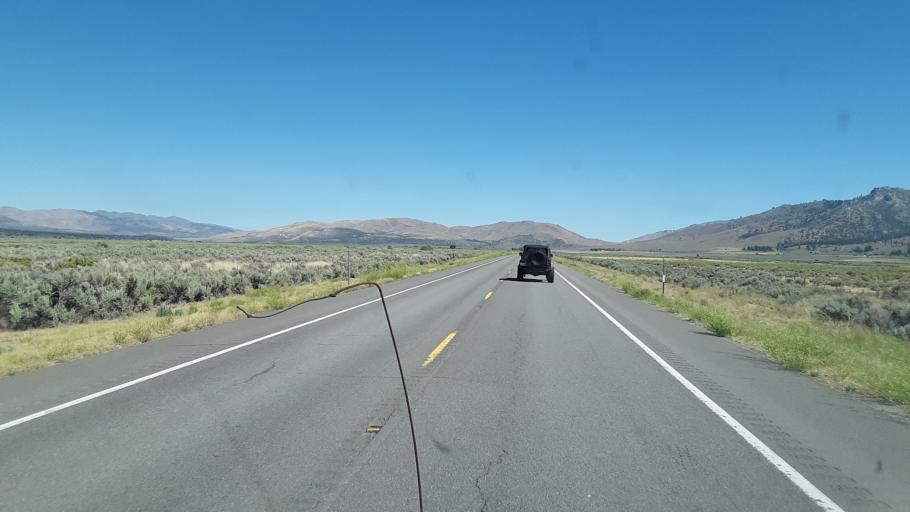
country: US
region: Nevada
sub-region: Washoe County
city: Cold Springs
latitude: 39.9880
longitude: -120.0709
